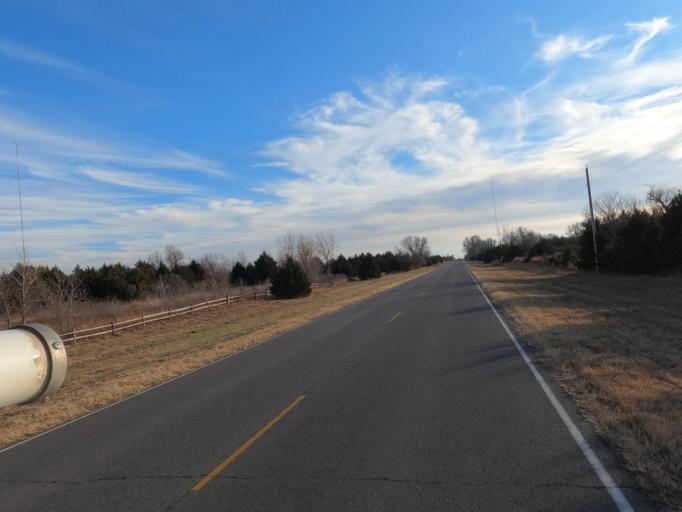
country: US
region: Kansas
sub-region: Reno County
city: Buhler
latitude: 38.0682
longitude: -97.7754
